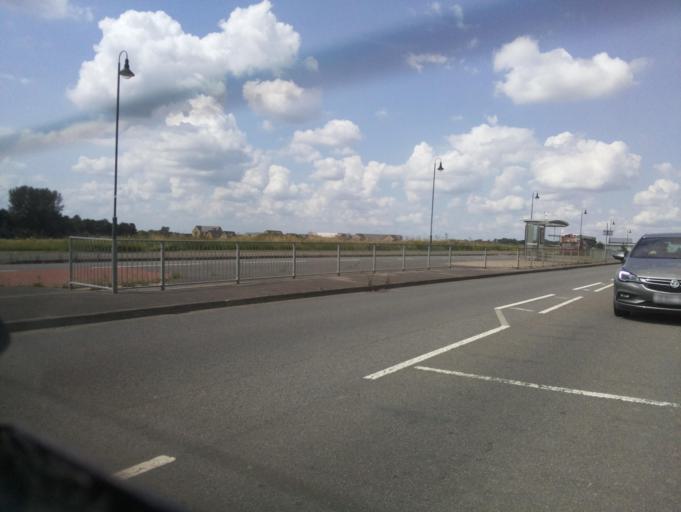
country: GB
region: England
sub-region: Borough of Swindon
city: Wroughton
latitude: 51.5437
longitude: -1.8032
